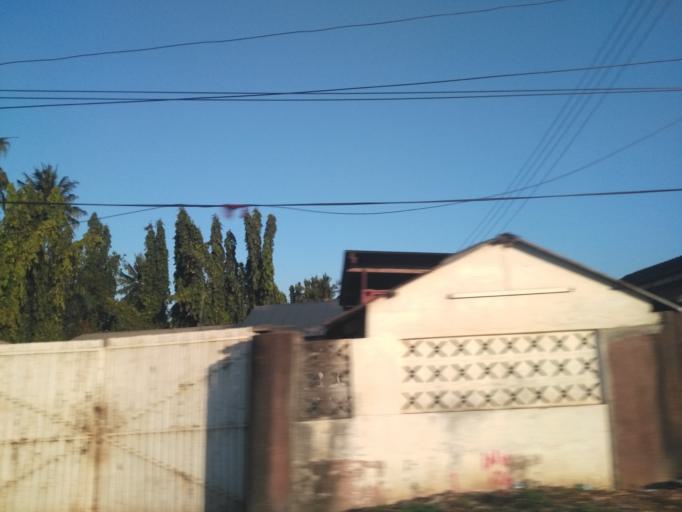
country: TZ
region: Dar es Salaam
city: Magomeni
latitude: -6.7554
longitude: 39.2359
